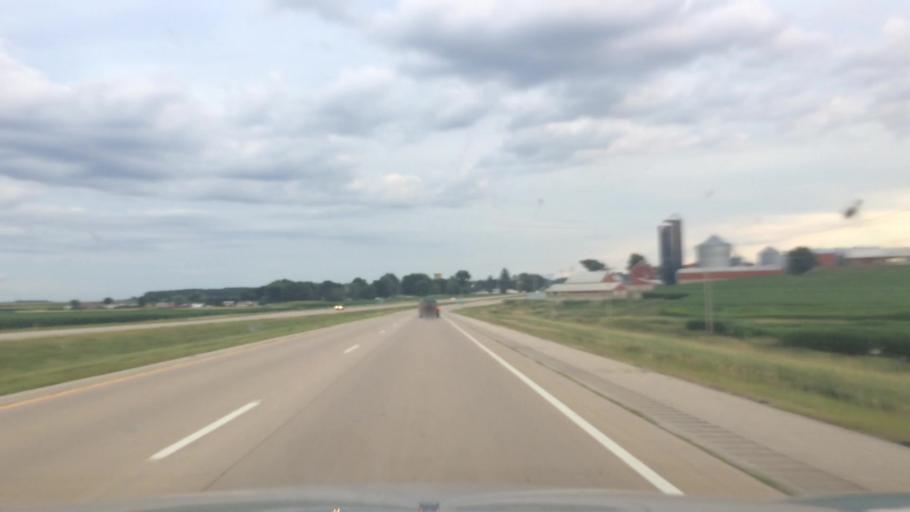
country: US
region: Wisconsin
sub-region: Dane County
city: Middleton
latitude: 43.1587
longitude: -89.5311
